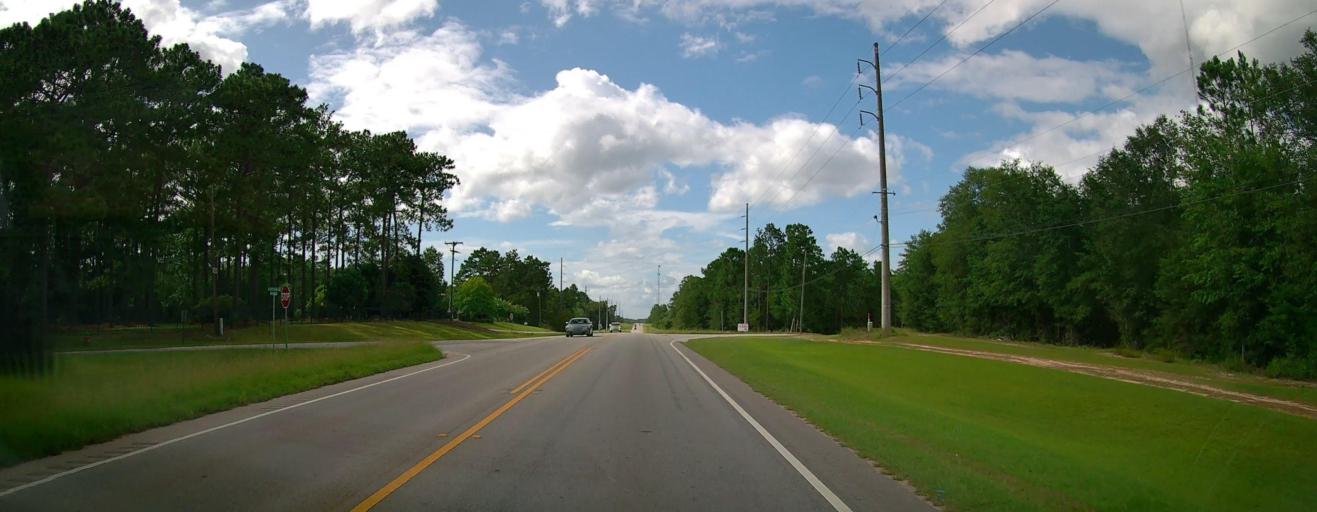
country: US
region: Georgia
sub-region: Coffee County
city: Douglas
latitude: 31.5217
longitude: -82.8729
